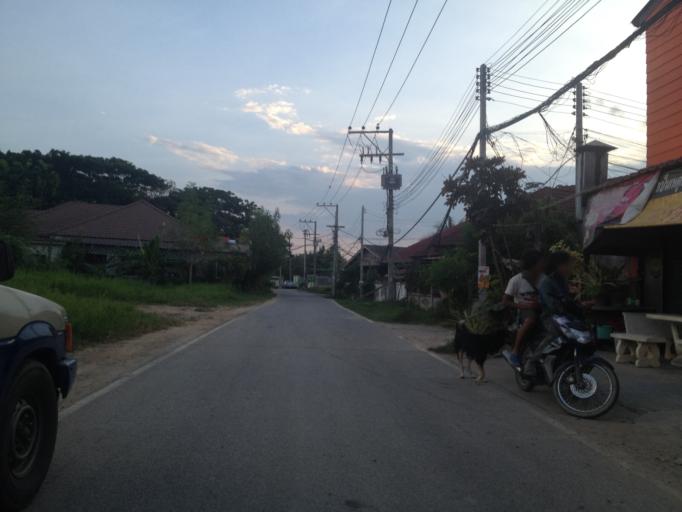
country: TH
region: Chiang Mai
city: Chiang Mai
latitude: 18.7612
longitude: 98.9590
